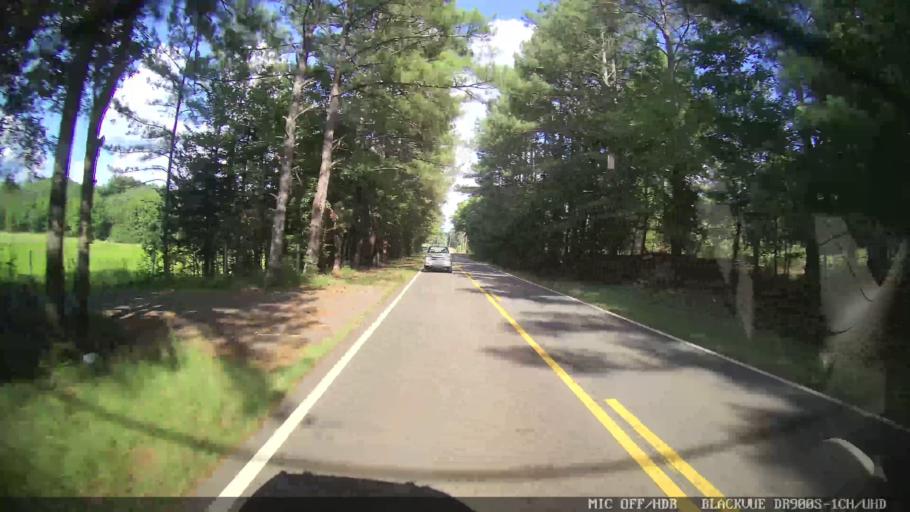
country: US
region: Georgia
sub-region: Bartow County
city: Euharlee
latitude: 34.1798
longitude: -85.0249
